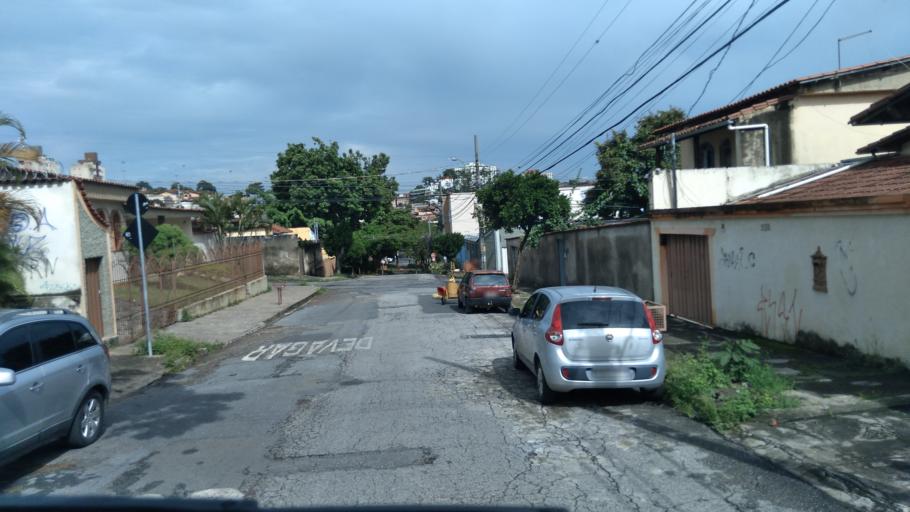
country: BR
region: Minas Gerais
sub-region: Contagem
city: Contagem
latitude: -19.9278
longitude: -44.0005
